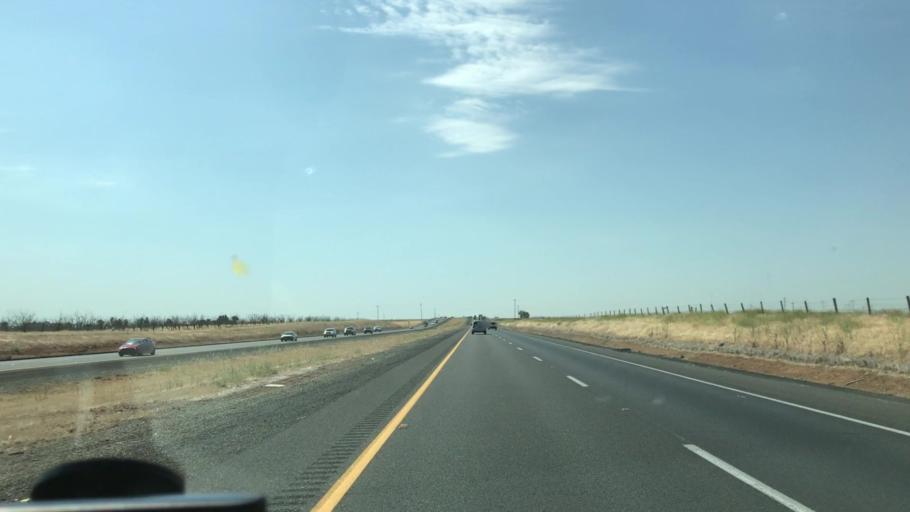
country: US
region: California
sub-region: Merced County
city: Los Banos
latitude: 37.0745
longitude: -120.9873
